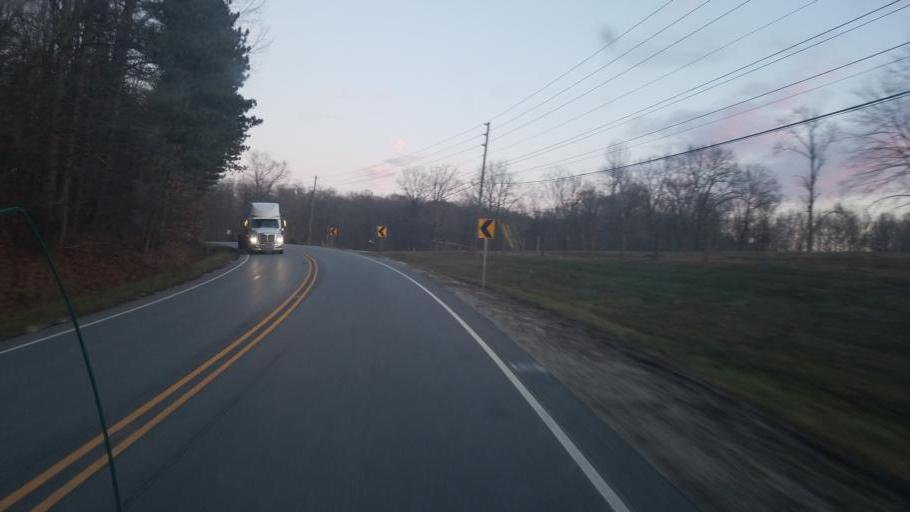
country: US
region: Indiana
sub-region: Lawrence County
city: Bedford
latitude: 38.8733
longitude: -86.3045
